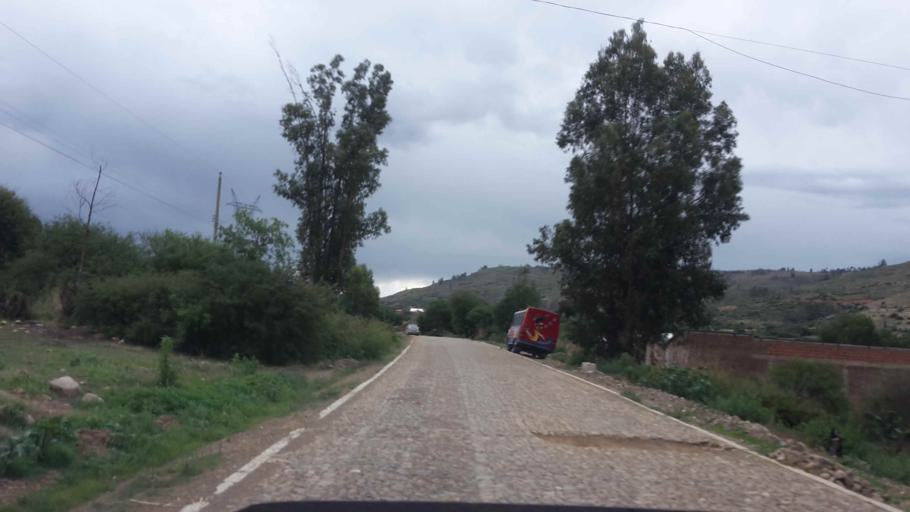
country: BO
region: Cochabamba
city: Cochabamba
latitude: -17.5442
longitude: -66.1902
